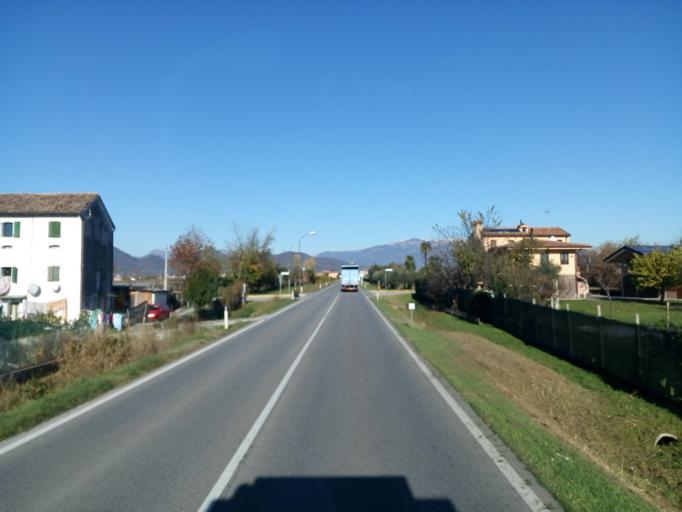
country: IT
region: Veneto
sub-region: Provincia di Treviso
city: Caerano di San Marco
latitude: 45.7720
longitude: 11.9942
